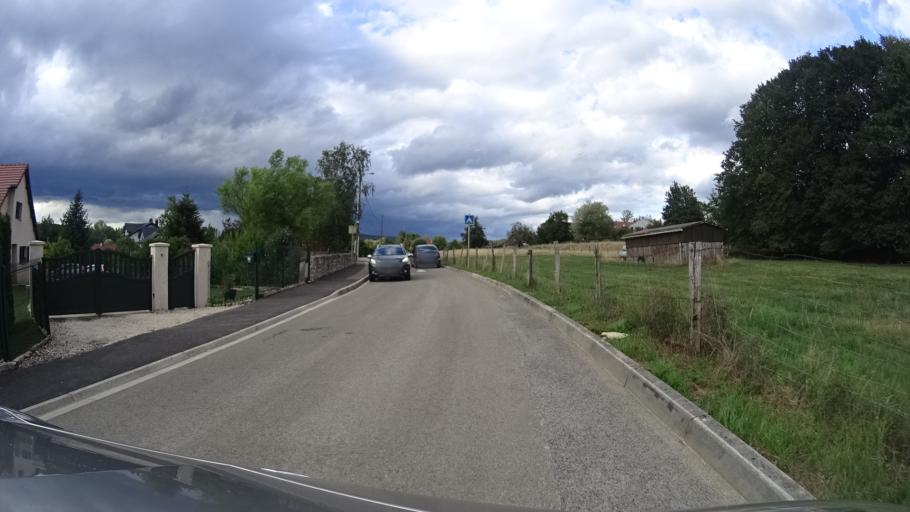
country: FR
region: Franche-Comte
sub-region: Departement du Doubs
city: Nancray
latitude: 47.2409
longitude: 6.1749
